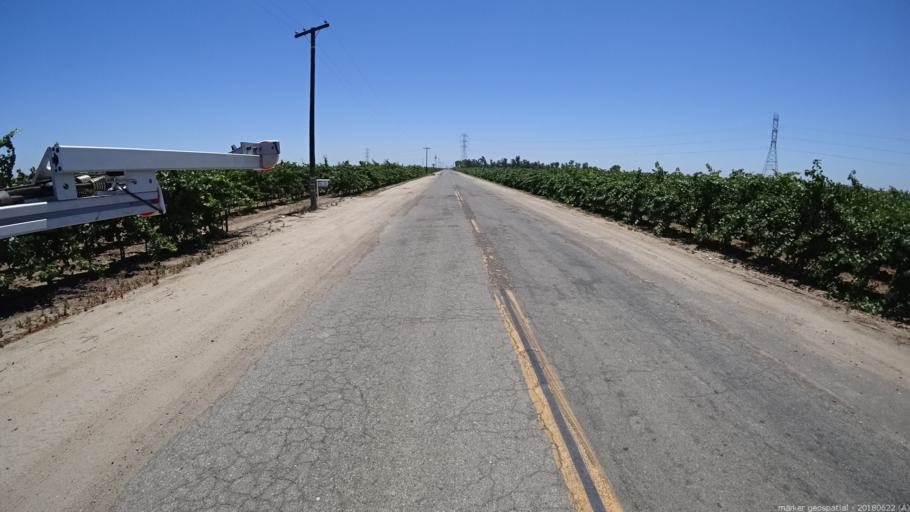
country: US
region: California
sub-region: Madera County
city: Parksdale
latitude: 36.9370
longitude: -119.9922
